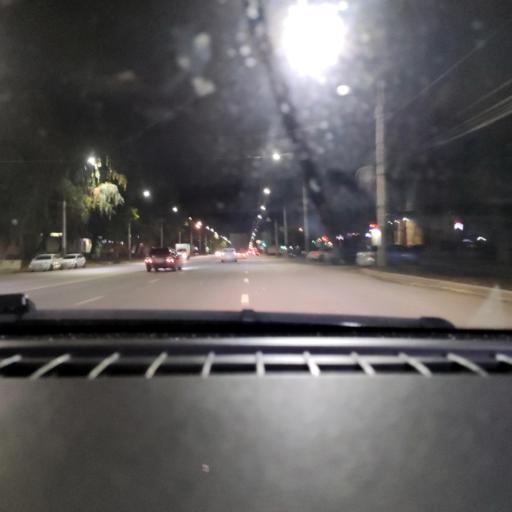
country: RU
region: Voronezj
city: Voronezh
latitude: 51.6415
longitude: 39.2365
